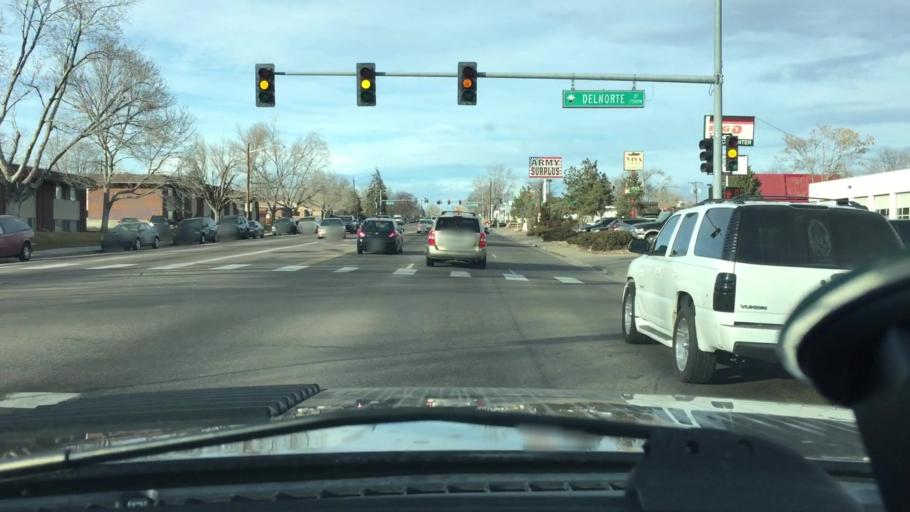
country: US
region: Colorado
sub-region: Adams County
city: Sherrelwood
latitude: 39.8324
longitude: -105.0061
